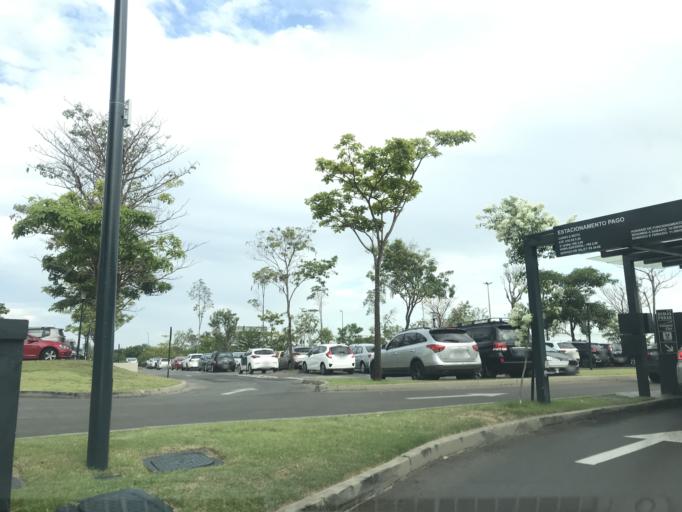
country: BR
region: Federal District
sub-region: Brasilia
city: Brasilia
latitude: -15.7212
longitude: -47.8871
